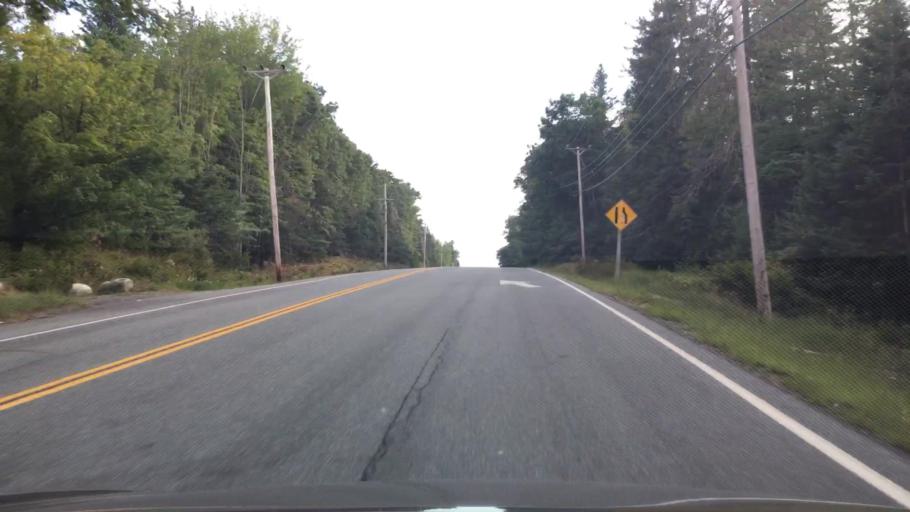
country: US
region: Maine
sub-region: Hancock County
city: Surry
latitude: 44.4898
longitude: -68.5100
